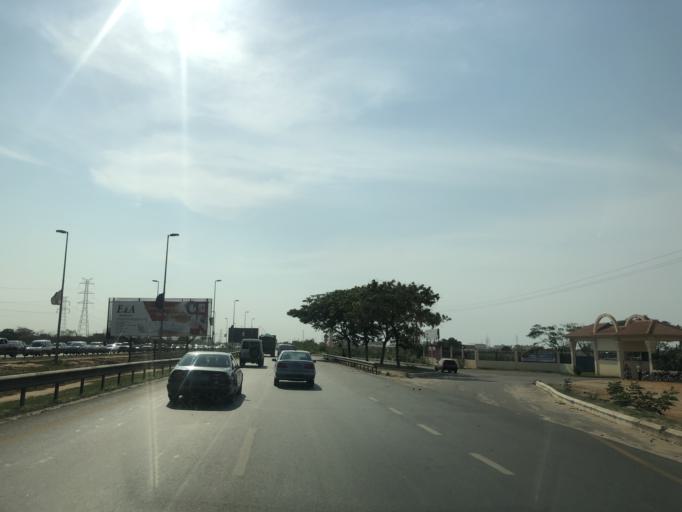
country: AO
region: Luanda
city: Luanda
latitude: -8.9733
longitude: 13.2710
